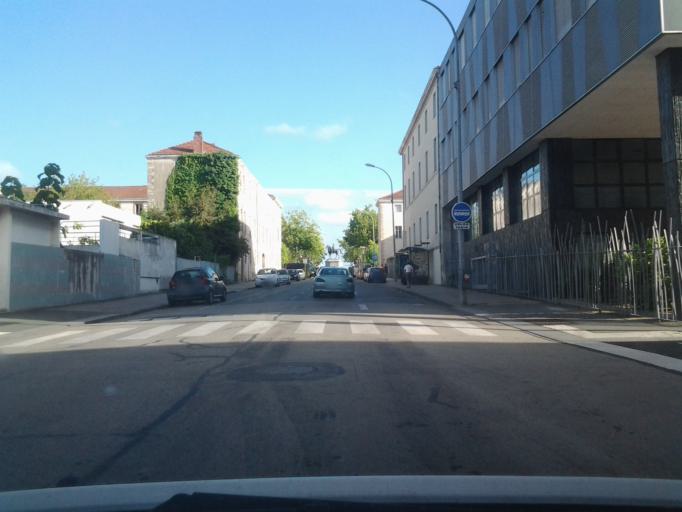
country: FR
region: Pays de la Loire
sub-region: Departement de la Vendee
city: La Roche-sur-Yon
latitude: 46.6721
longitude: -1.4275
